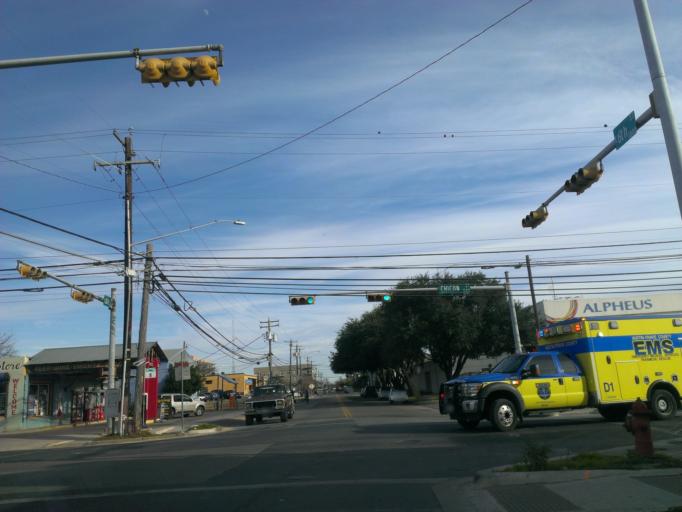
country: US
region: Texas
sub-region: Travis County
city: Austin
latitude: 30.2617
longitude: -97.7228
